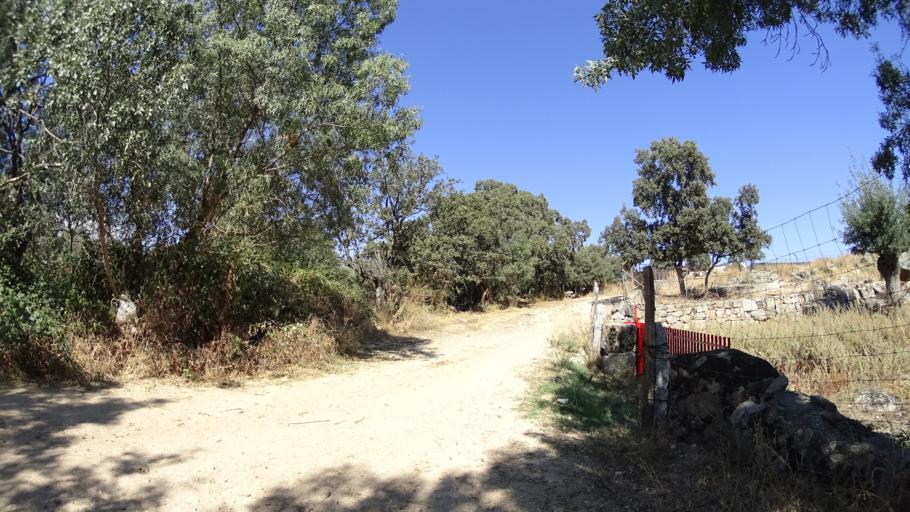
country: ES
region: Madrid
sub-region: Provincia de Madrid
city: Collado-Villalba
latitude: 40.6113
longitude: -4.0032
